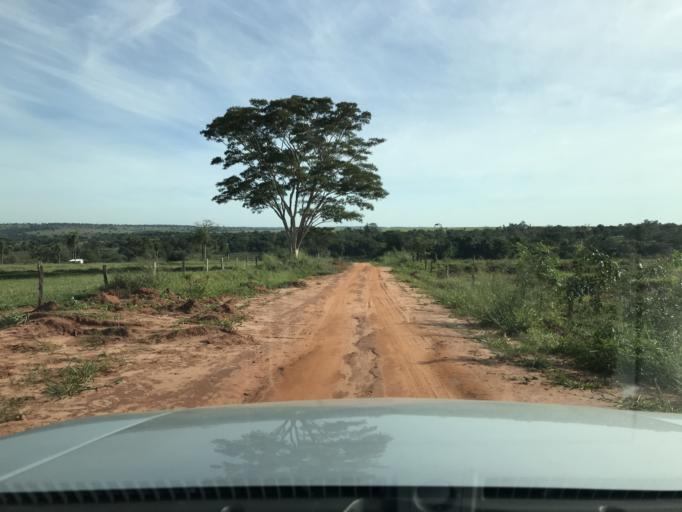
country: BR
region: Mato Grosso do Sul
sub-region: Iguatemi
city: Iguatemi
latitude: -23.6496
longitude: -54.5752
